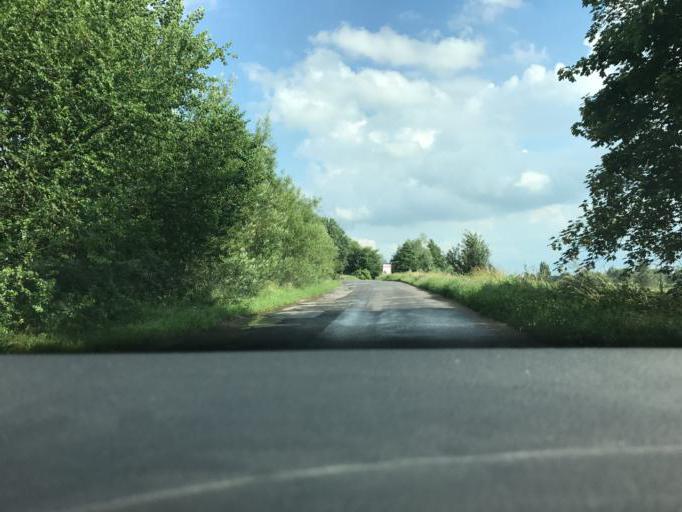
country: PL
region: Pomeranian Voivodeship
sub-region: Powiat gdanski
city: Cedry Wielkie
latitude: 54.3414
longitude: 18.7950
